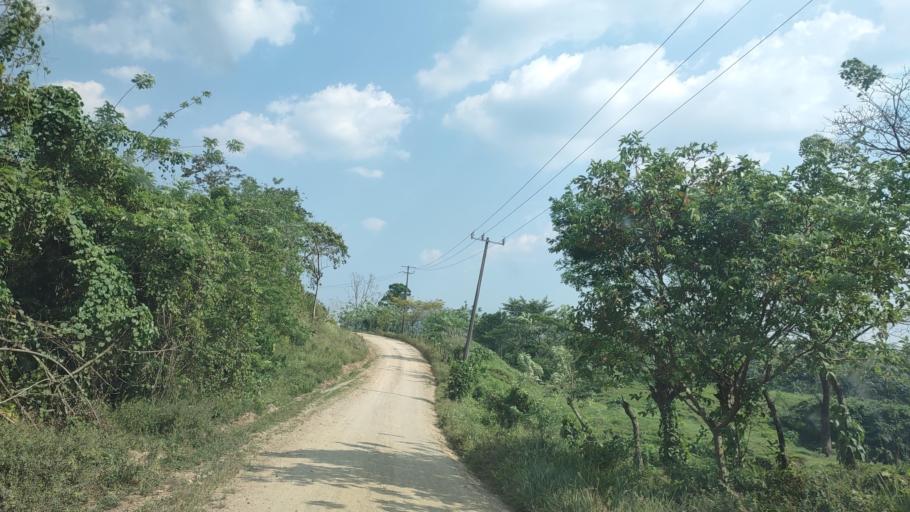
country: MX
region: Chiapas
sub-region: Tecpatan
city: Raudales Malpaso
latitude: 17.3329
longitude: -93.7507
